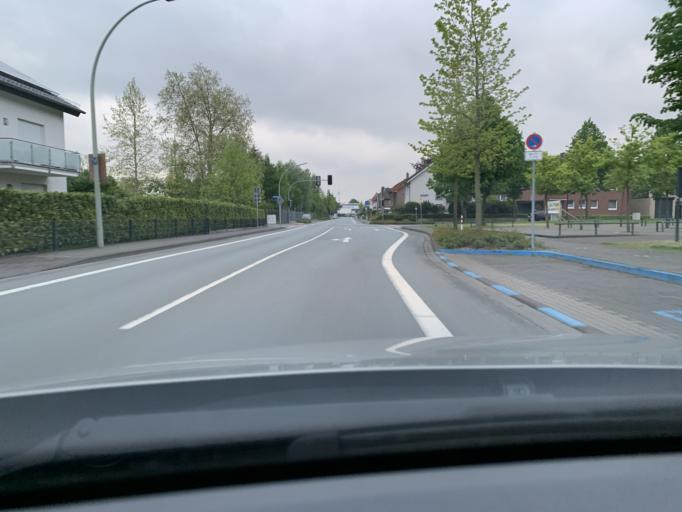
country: DE
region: North Rhine-Westphalia
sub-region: Regierungsbezirk Detmold
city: Rheda-Wiedenbruck
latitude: 51.8280
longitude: 8.3034
